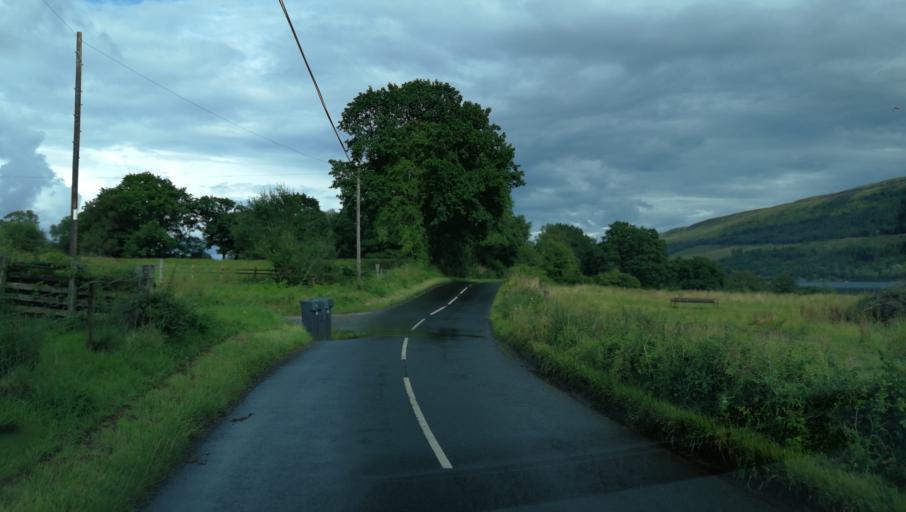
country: GB
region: Scotland
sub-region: Stirling
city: Callander
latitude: 56.2259
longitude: -4.2976
